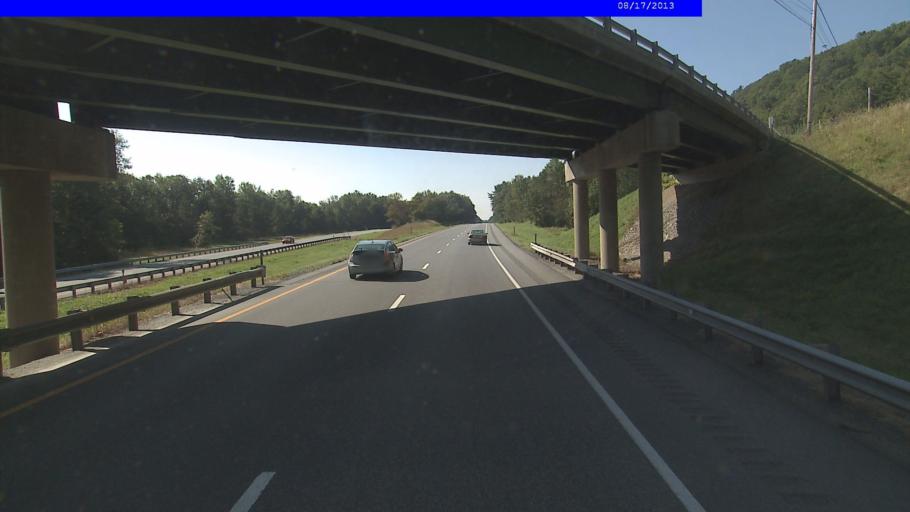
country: US
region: Vermont
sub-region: Windsor County
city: Windsor
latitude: 43.5659
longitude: -72.3857
